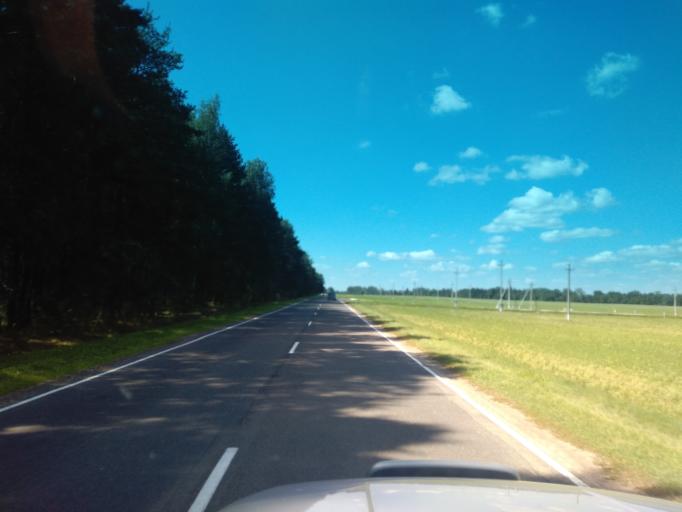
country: BY
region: Minsk
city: Stan'kava
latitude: 53.6247
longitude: 27.2785
